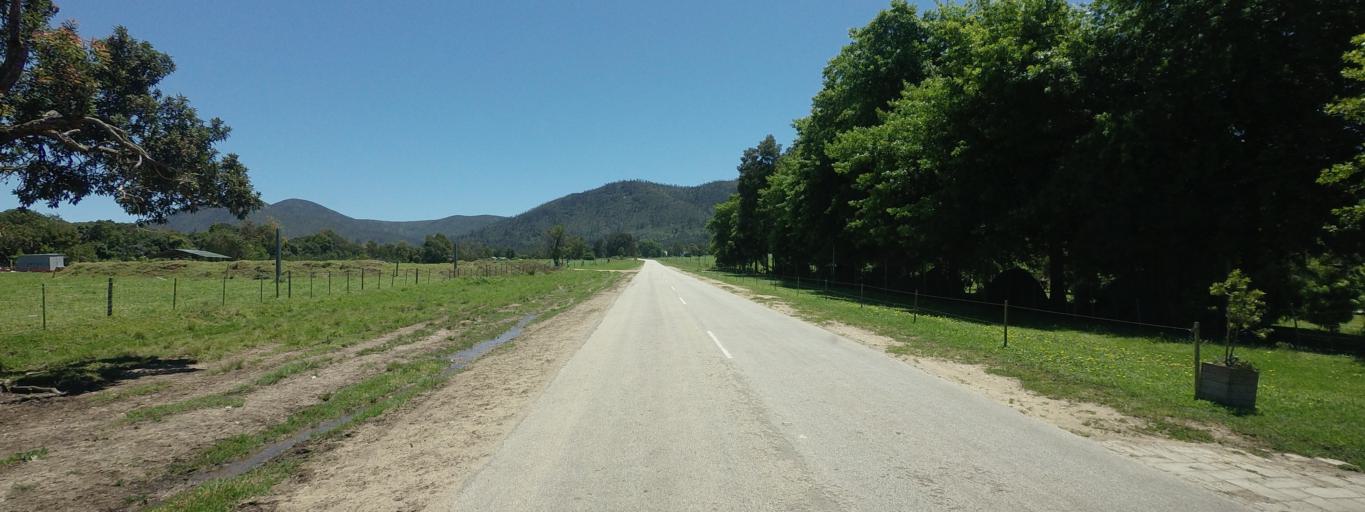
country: ZA
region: Western Cape
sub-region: Eden District Municipality
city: Plettenberg Bay
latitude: -33.9426
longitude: 23.5114
